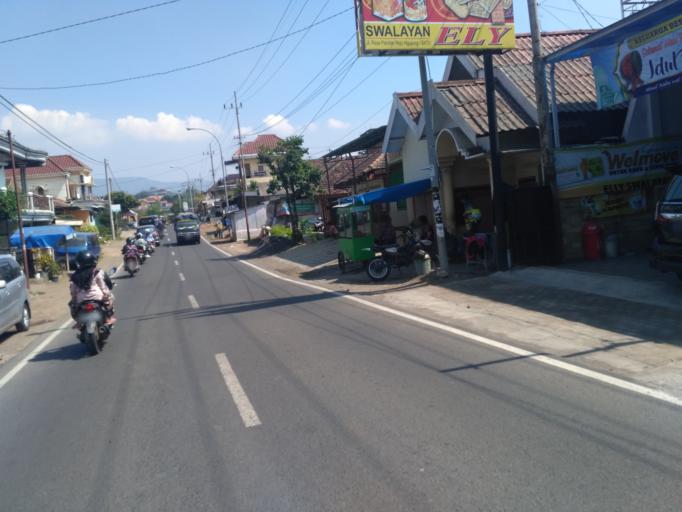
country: ID
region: East Java
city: Batu
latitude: -7.8642
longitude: 112.5512
